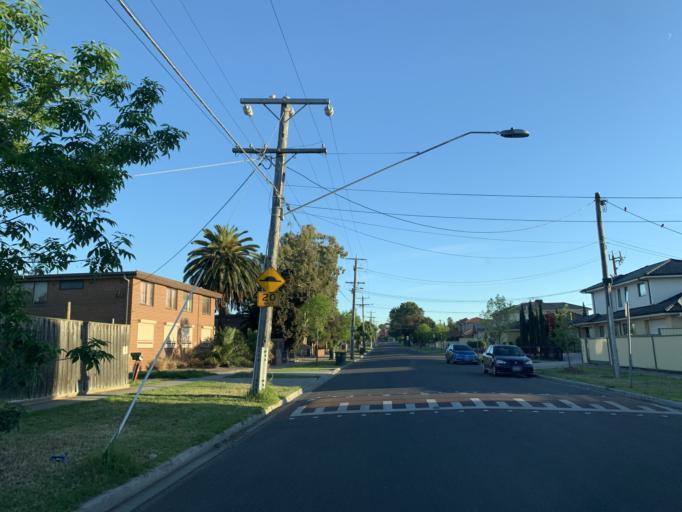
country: AU
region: Victoria
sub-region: Brimbank
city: St Albans
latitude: -37.7477
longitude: 144.8041
